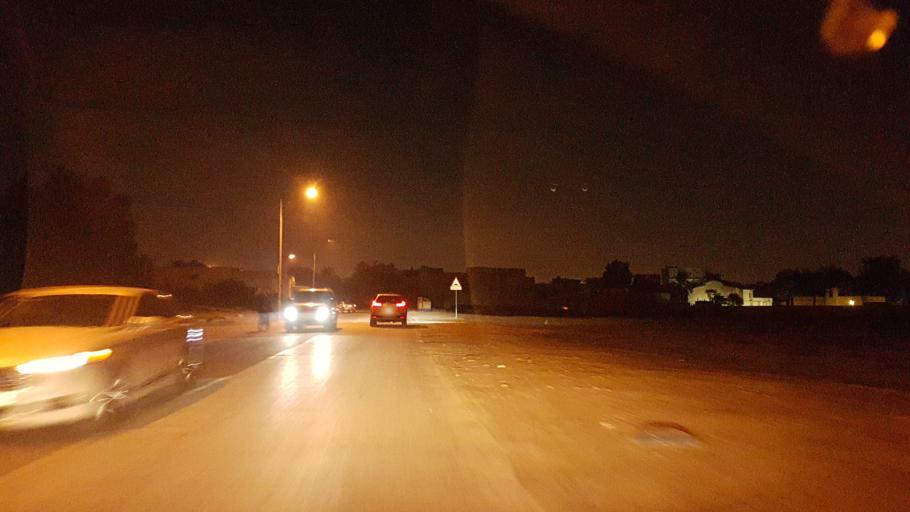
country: BH
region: Manama
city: Jidd Hafs
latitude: 26.2308
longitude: 50.4999
